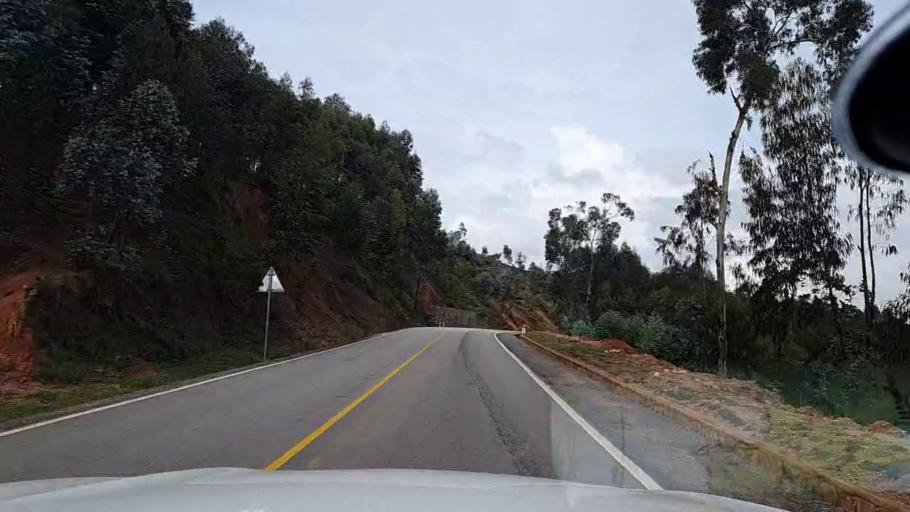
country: RW
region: Southern Province
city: Nzega
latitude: -2.5053
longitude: 29.5034
